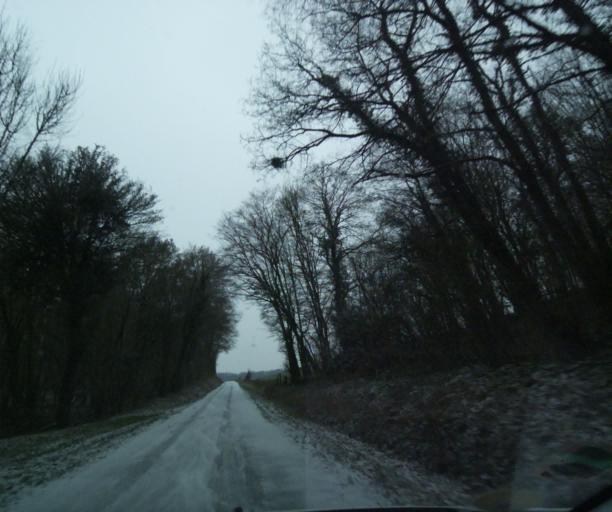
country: FR
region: Champagne-Ardenne
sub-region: Departement de la Haute-Marne
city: Bienville
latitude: 48.4817
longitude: 5.0452
